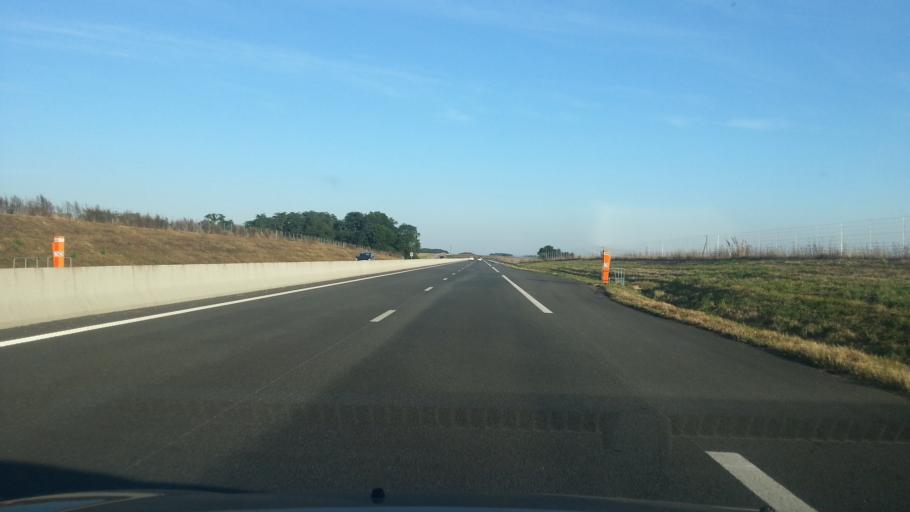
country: FR
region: Picardie
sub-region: Departement de l'Oise
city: Catenoy
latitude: 49.3843
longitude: 2.4976
